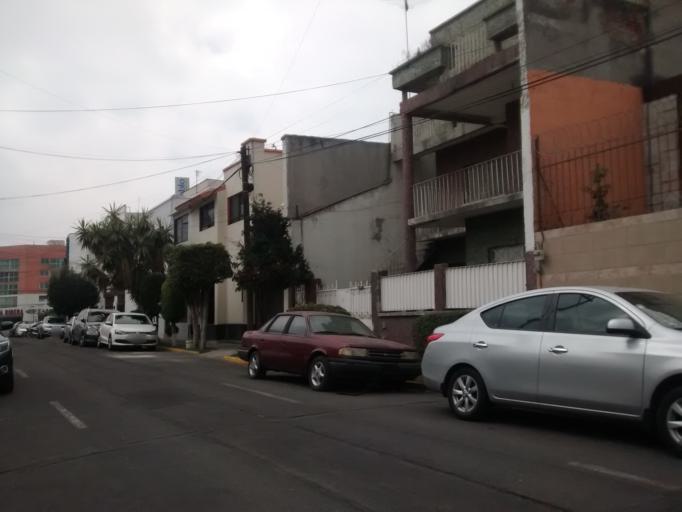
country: MX
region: Mexico
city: Colonia Lindavista
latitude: 19.4923
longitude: -99.1359
